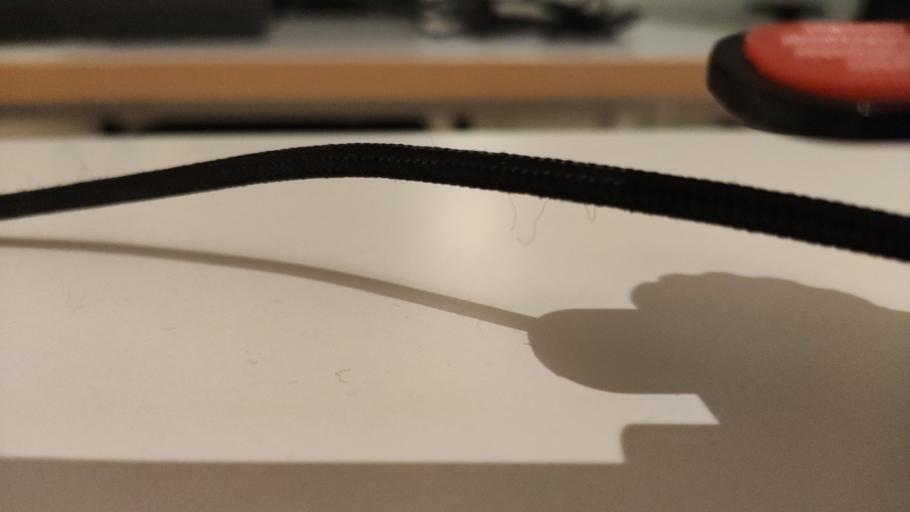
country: RU
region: Moskovskaya
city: Budenovetc
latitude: 56.3918
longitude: 37.6297
